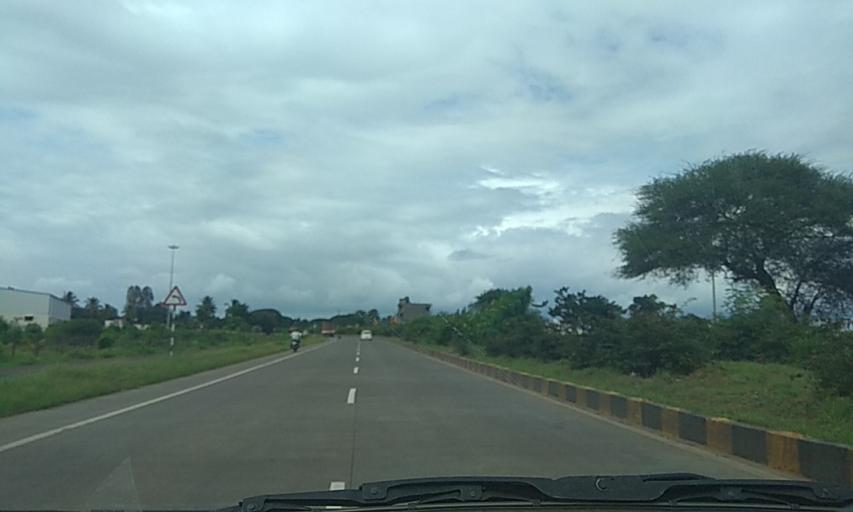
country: IN
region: Maharashtra
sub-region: Kolhapur
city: Kagal
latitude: 16.5640
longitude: 74.3165
